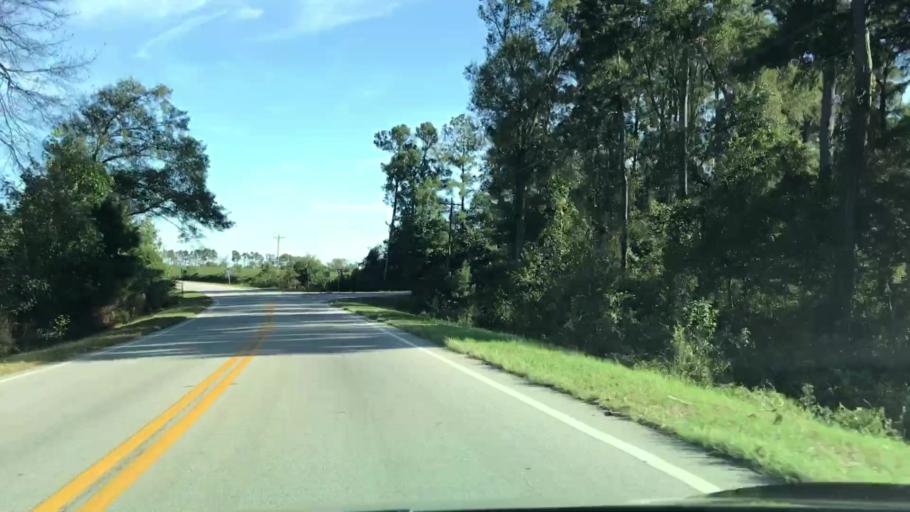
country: US
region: Georgia
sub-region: Glascock County
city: Gibson
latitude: 33.3207
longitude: -82.5574
